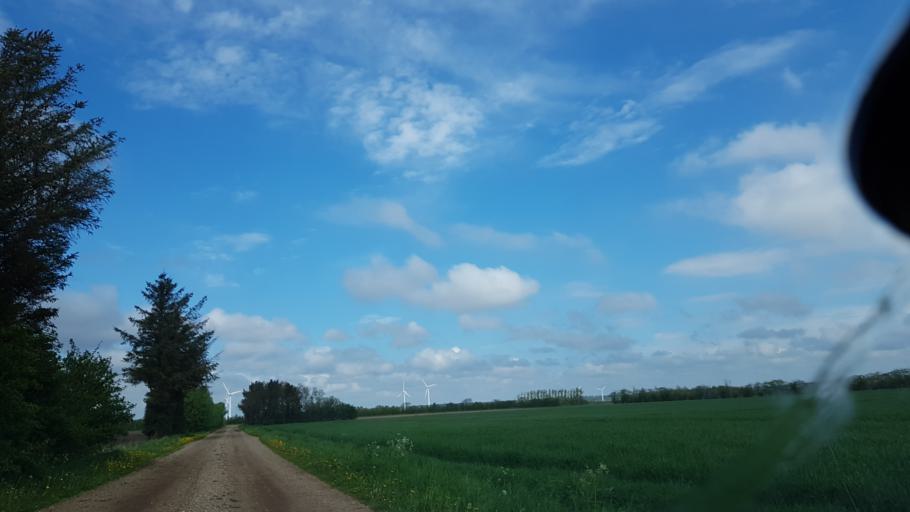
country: DK
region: South Denmark
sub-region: Tonder Kommune
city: Sherrebek
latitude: 55.0867
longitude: 8.8455
